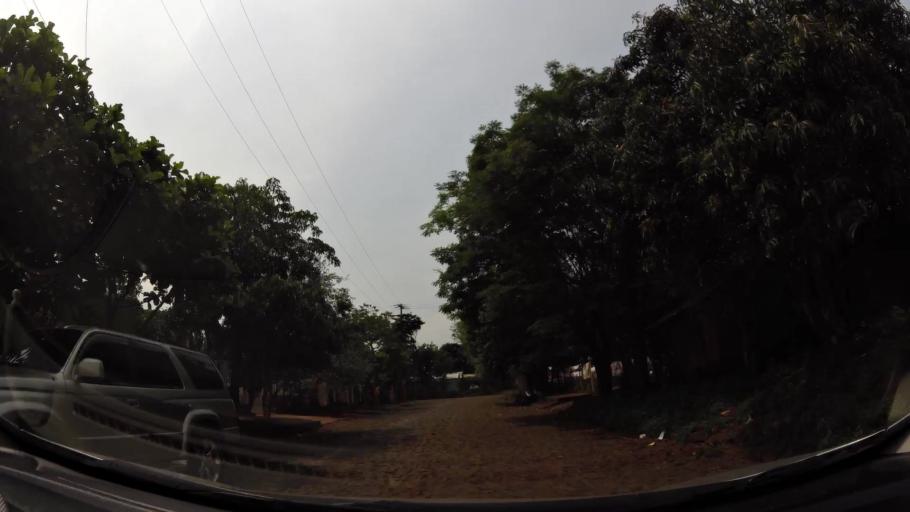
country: PY
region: Alto Parana
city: Presidente Franco
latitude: -25.5676
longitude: -54.6169
